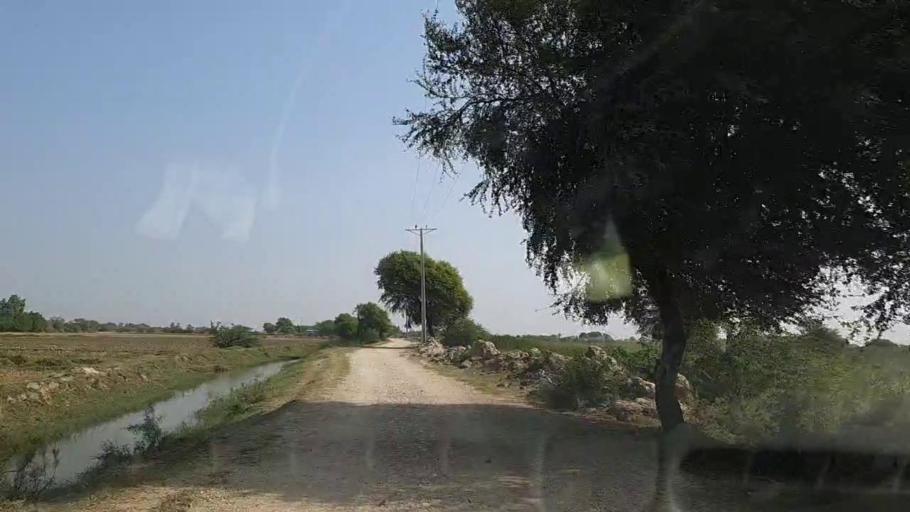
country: PK
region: Sindh
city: Mirpur Sakro
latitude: 24.5266
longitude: 67.8052
